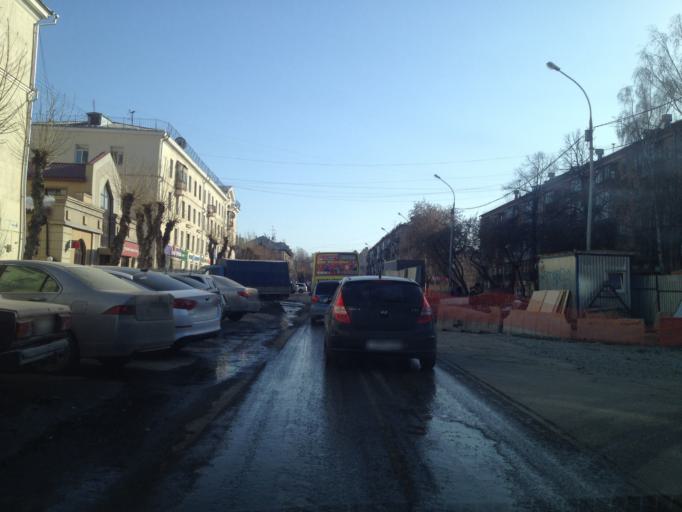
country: RU
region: Sverdlovsk
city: Yekaterinburg
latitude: 56.8373
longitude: 60.5535
